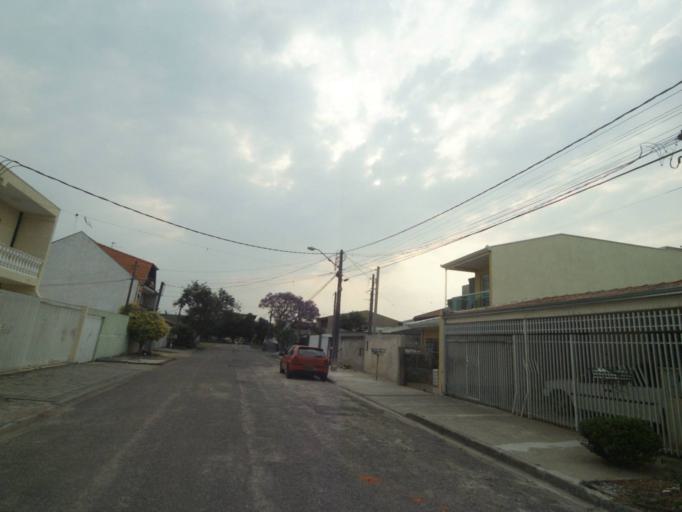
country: BR
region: Parana
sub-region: Sao Jose Dos Pinhais
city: Sao Jose dos Pinhais
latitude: -25.5346
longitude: -49.2508
